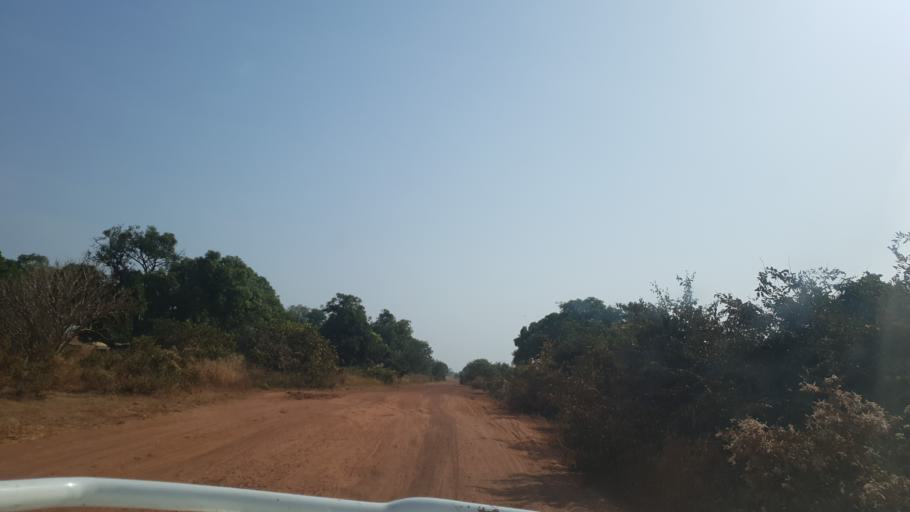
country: ML
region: Koulikoro
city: Dioila
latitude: 12.6686
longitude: -6.6802
